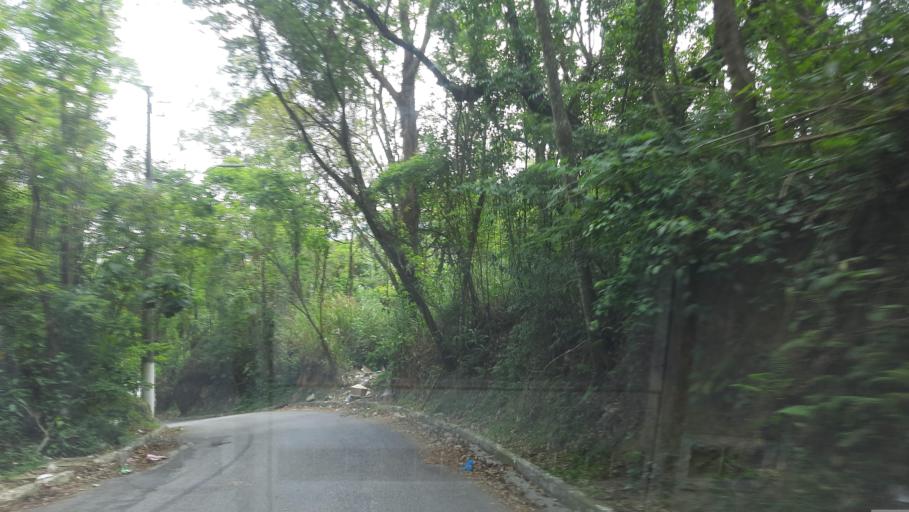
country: BR
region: Sao Paulo
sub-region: Caieiras
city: Caieiras
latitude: -23.4204
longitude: -46.7236
